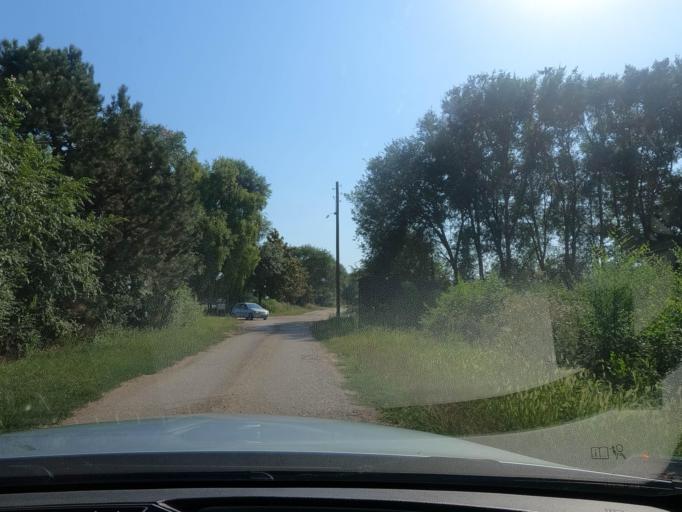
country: RS
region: Autonomna Pokrajina Vojvodina
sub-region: Juznobacki Okrug
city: Becej
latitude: 45.6556
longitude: 19.9001
